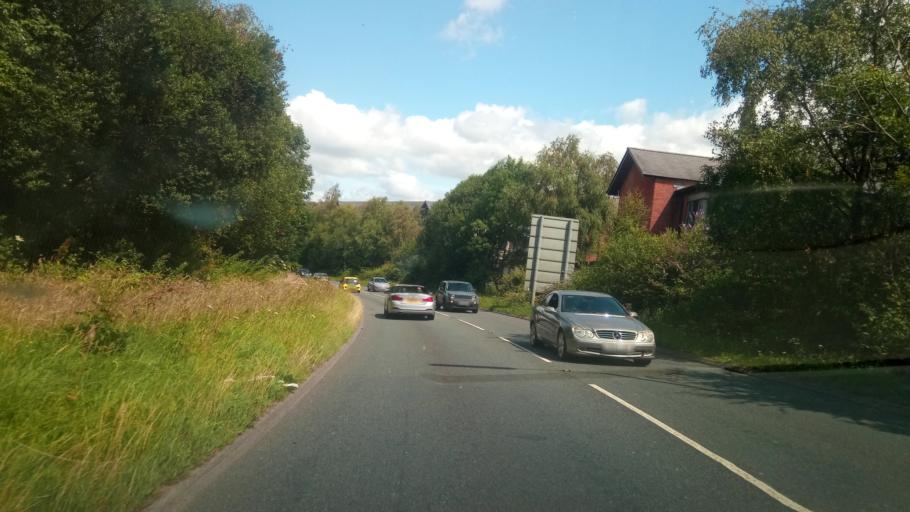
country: GB
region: Wales
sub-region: Caerphilly County Borough
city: Caerphilly
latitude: 51.5713
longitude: -3.2464
